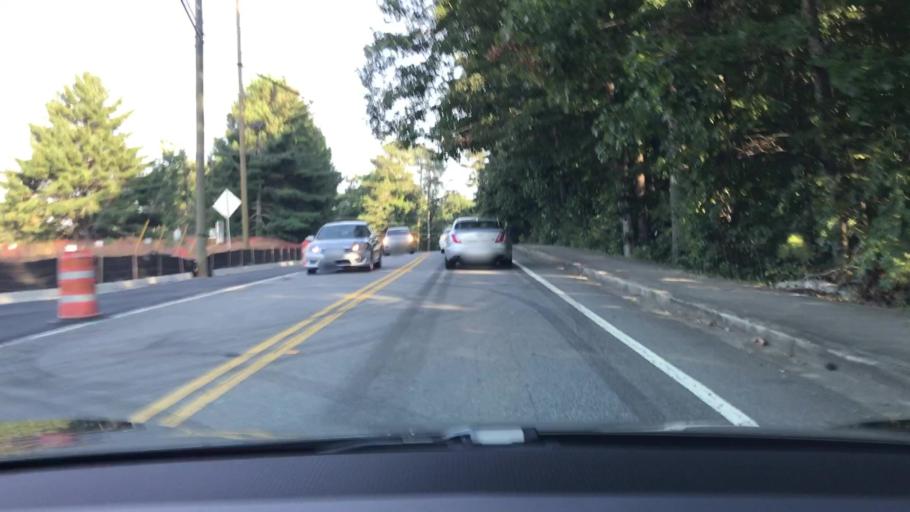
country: US
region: Georgia
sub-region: Fulton County
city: Alpharetta
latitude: 34.0745
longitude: -84.2365
